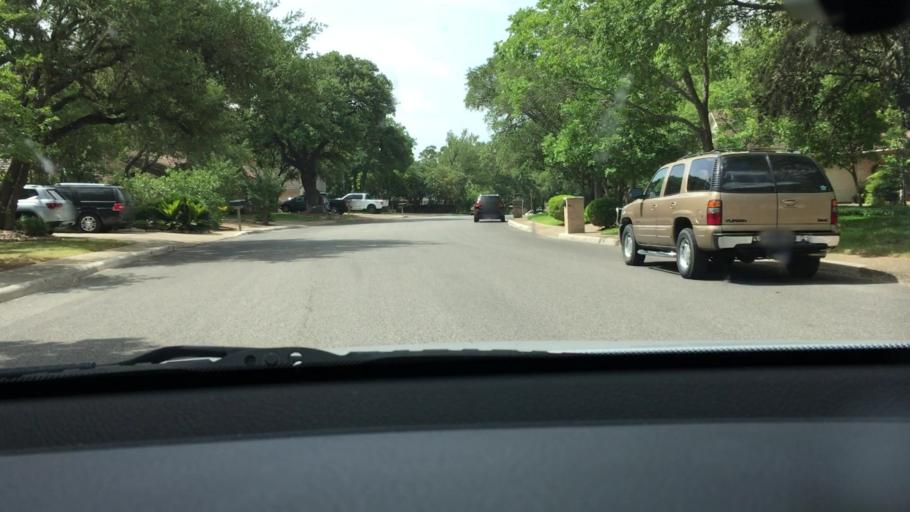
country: US
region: Texas
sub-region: Bexar County
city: Hollywood Park
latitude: 29.6280
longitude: -98.4550
